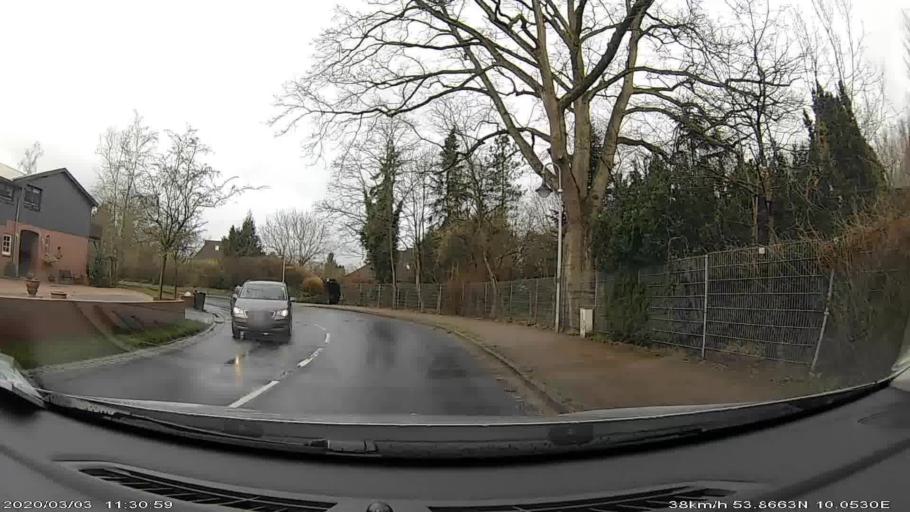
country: DE
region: Schleswig-Holstein
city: Struvenhutten
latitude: 53.8658
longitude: 10.0507
